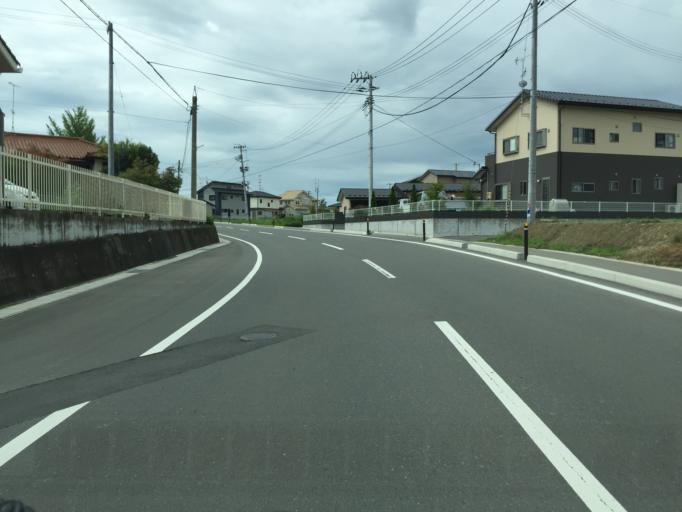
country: JP
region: Miyagi
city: Marumori
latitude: 37.8199
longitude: 140.9474
